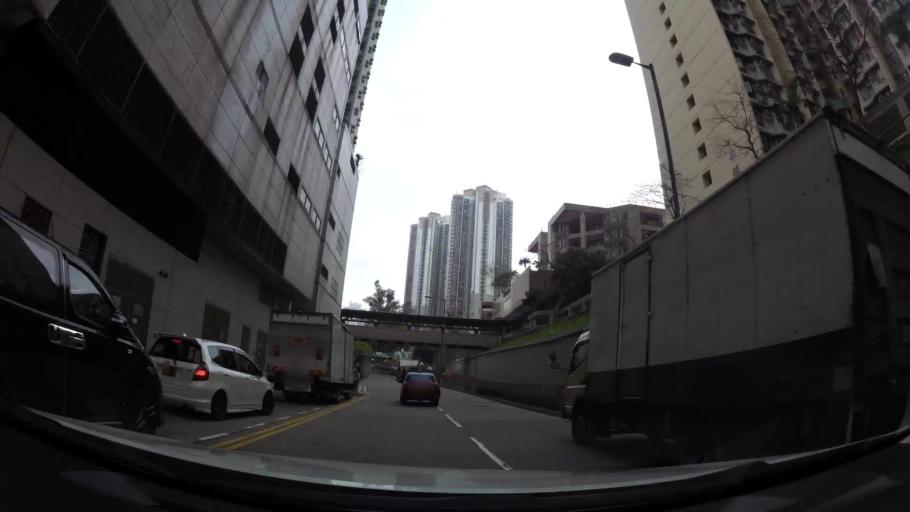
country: HK
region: Kowloon City
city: Kowloon
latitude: 22.3075
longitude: 114.2357
